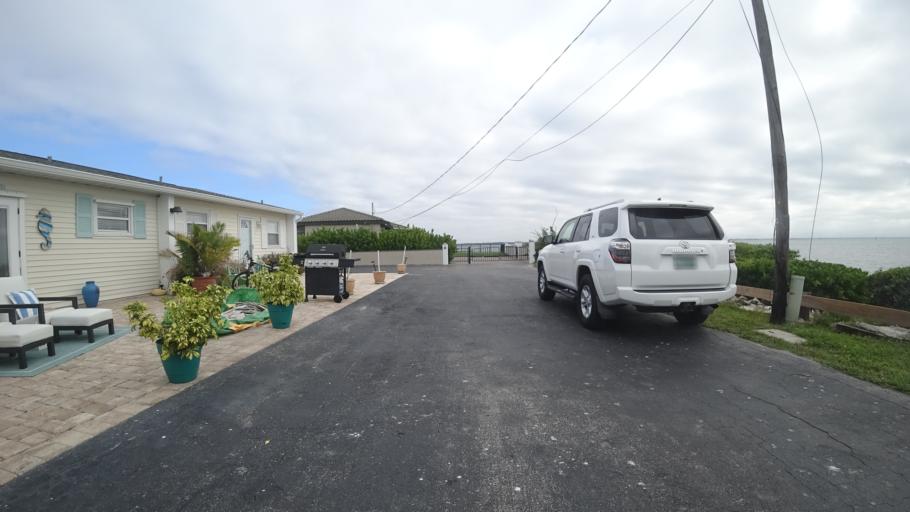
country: US
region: Florida
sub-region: Manatee County
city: Longboat Key
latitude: 27.4176
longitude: -82.6549
